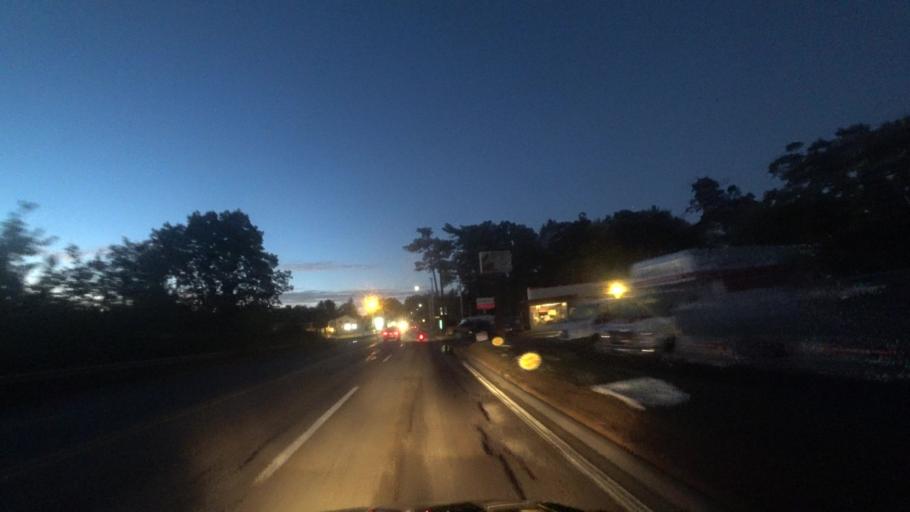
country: US
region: Massachusetts
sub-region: Middlesex County
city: North Reading
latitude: 42.5996
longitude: -71.1213
